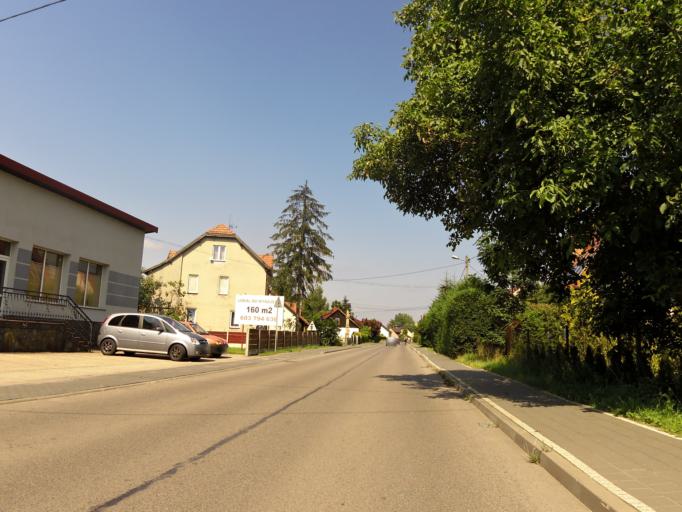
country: PL
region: Silesian Voivodeship
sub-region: Powiat zywiecki
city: Wegierska Gorka
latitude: 49.6150
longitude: 19.1303
